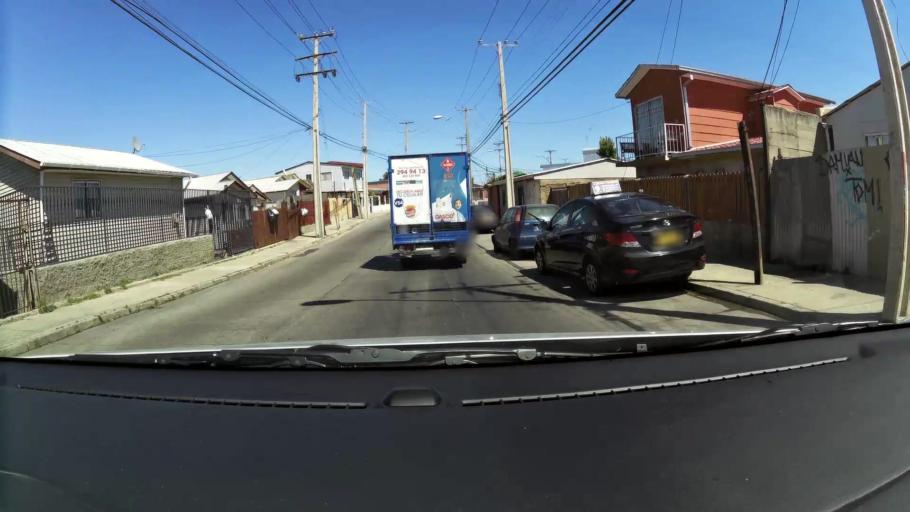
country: CL
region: Valparaiso
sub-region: Provincia de Valparaiso
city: Vina del Mar
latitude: -33.0525
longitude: -71.5831
